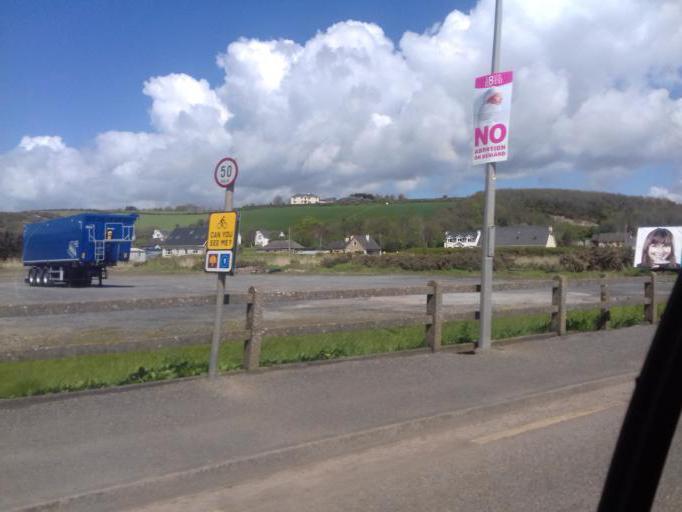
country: IE
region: Munster
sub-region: Waterford
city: Dunmore East
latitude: 52.2428
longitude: -6.9545
